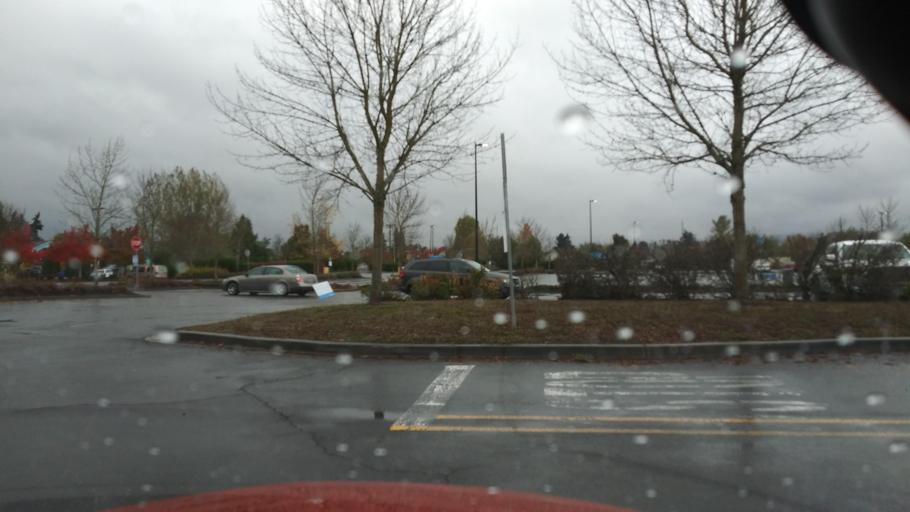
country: US
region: Oregon
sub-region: Washington County
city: Cornelius
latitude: 45.5228
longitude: -123.0678
